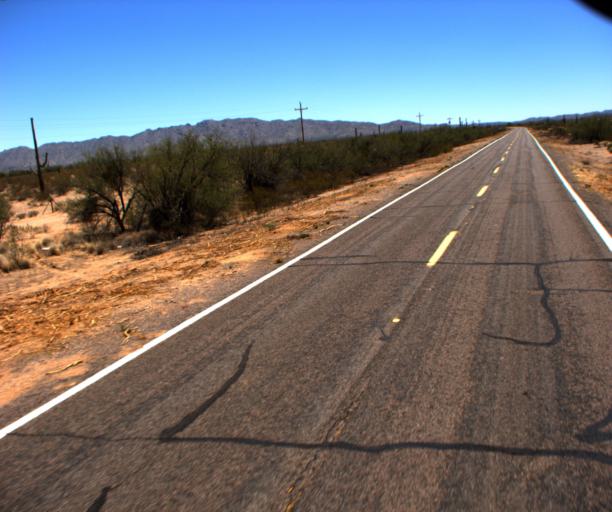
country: US
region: Arizona
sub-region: Pima County
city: Sells
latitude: 32.1813
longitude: -112.3254
